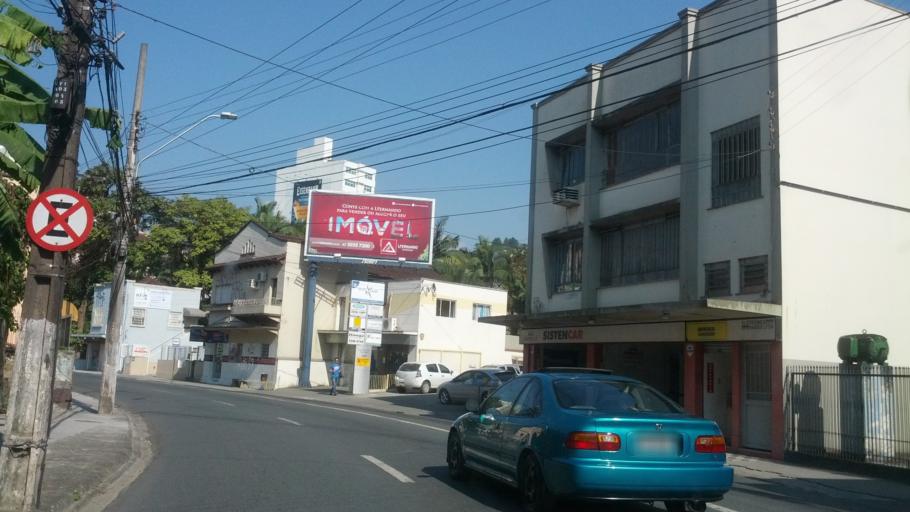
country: BR
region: Santa Catarina
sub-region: Blumenau
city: Blumenau
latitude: -26.9131
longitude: -49.0712
